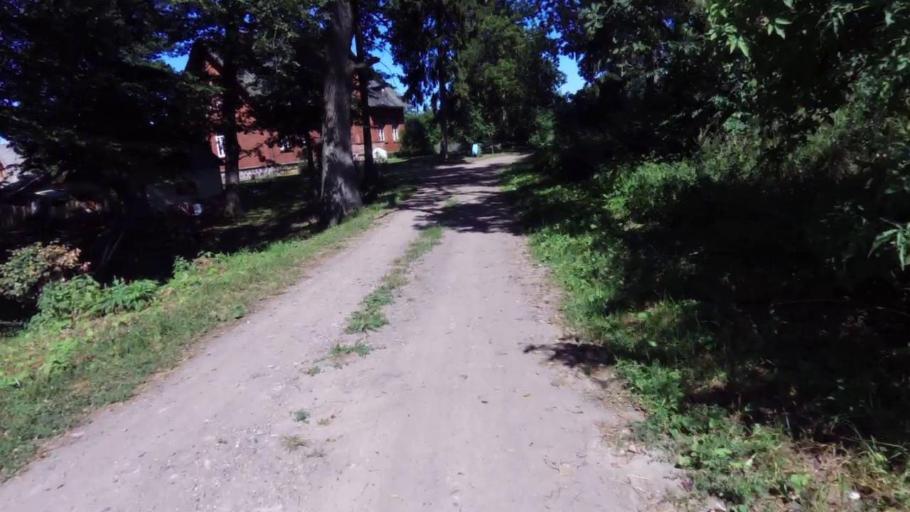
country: PL
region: West Pomeranian Voivodeship
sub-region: Powiat drawski
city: Wierzchowo
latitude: 53.5253
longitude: 16.1411
